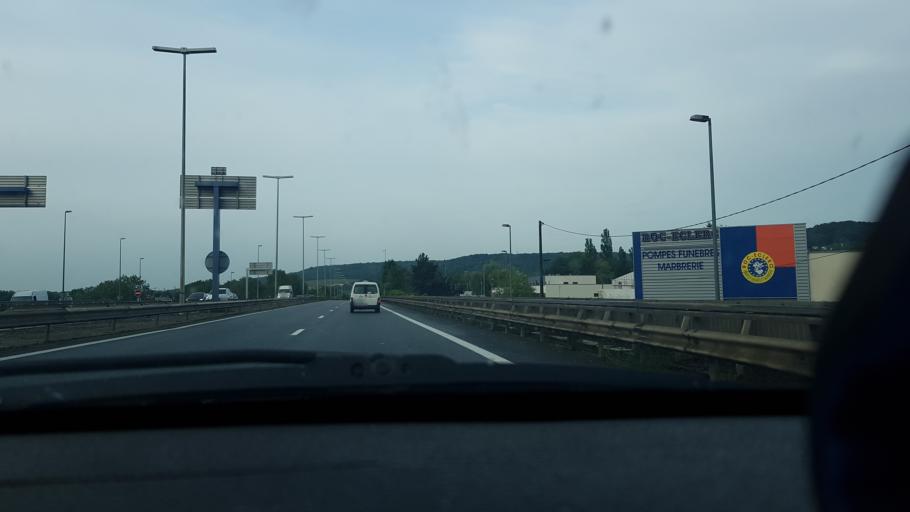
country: FR
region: Lorraine
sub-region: Departement de Meurthe-et-Moselle
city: Vandoeuvre-les-Nancy
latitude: 48.6601
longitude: 6.1868
